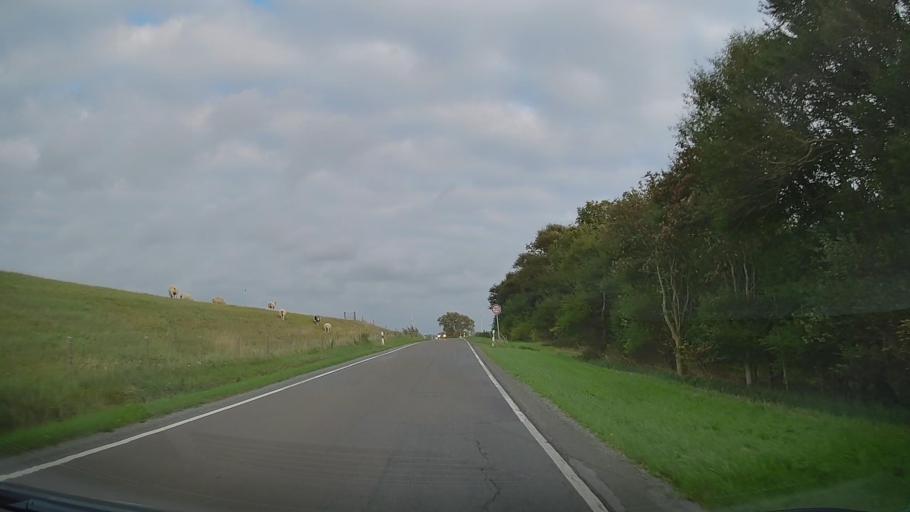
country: DE
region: Schleswig-Holstein
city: Uelvesbull
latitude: 54.4155
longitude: 8.9154
